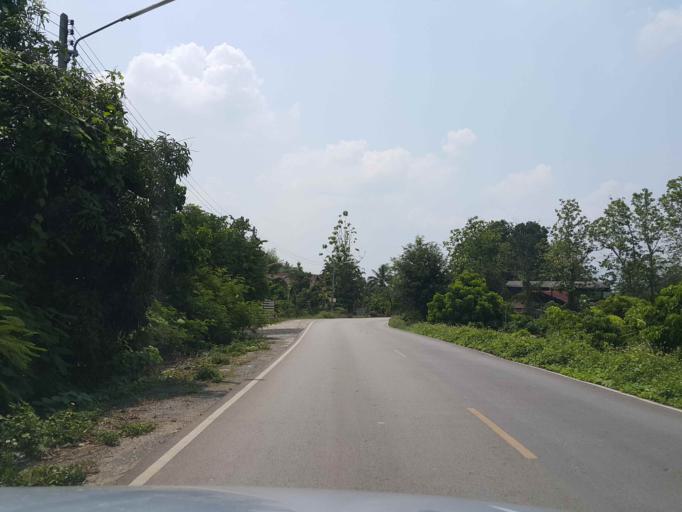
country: TH
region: Chiang Mai
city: Saraphi
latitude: 18.6827
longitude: 99.0001
